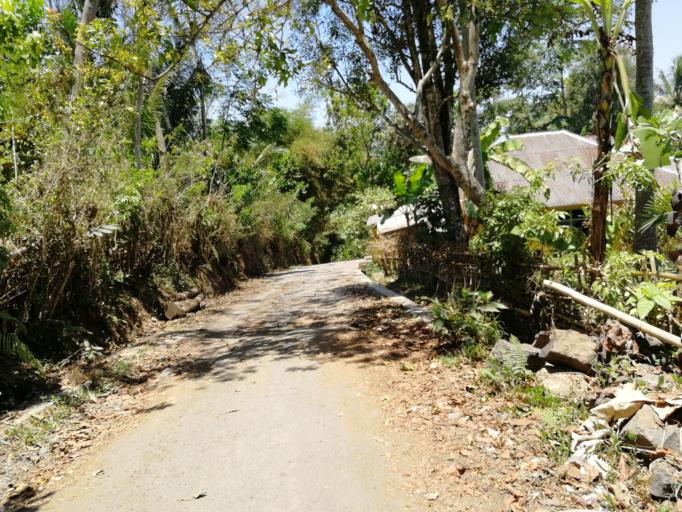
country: ID
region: West Nusa Tenggara
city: Tetebatu
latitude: -8.5497
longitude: 116.4193
